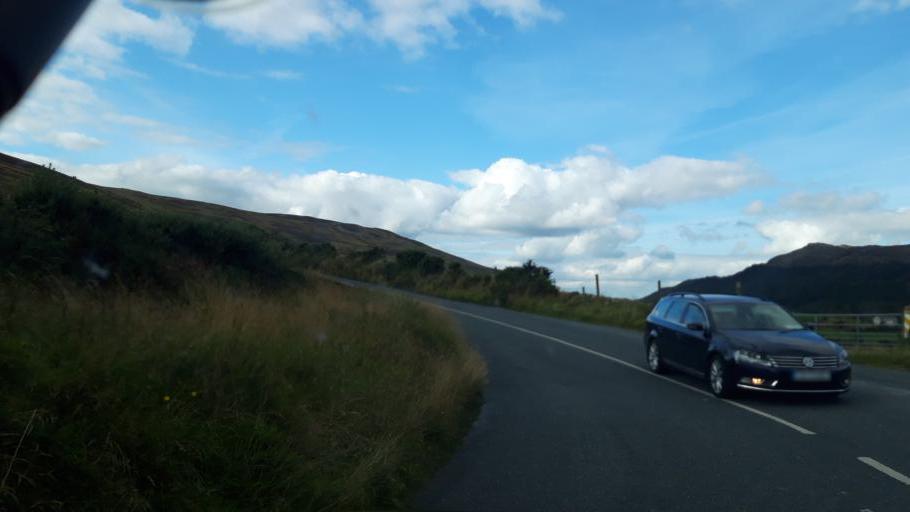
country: GB
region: Northern Ireland
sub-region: Down District
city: Warrenpoint
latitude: 54.0408
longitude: -6.2669
